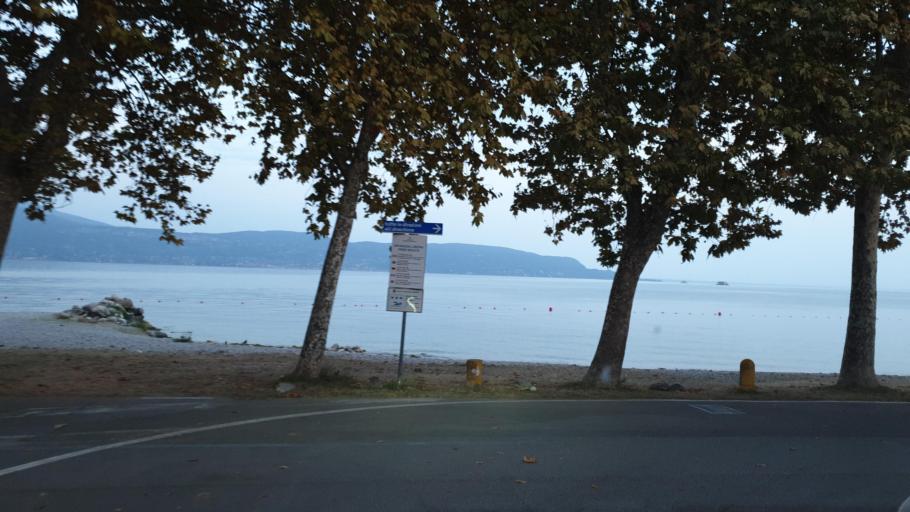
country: IT
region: Lombardy
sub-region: Provincia di Brescia
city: Toscolano Maderno
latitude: 45.6372
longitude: 10.6181
